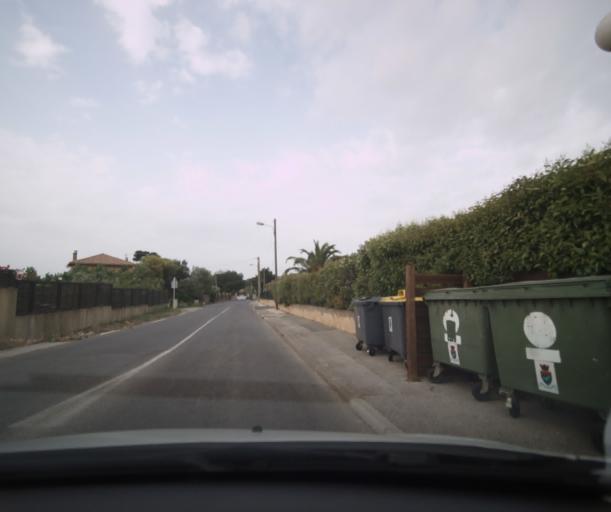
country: FR
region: Provence-Alpes-Cote d'Azur
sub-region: Departement du Var
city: Carqueiranne
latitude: 43.0971
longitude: 6.0794
